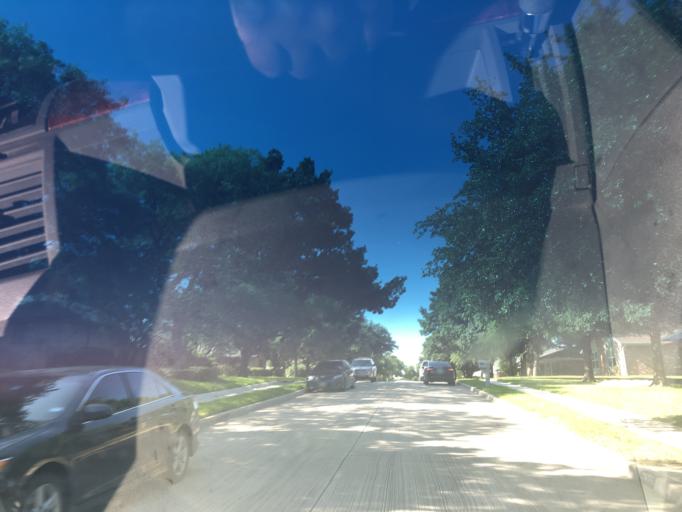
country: US
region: Texas
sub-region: Dallas County
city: Grand Prairie
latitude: 32.7174
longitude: -97.0180
